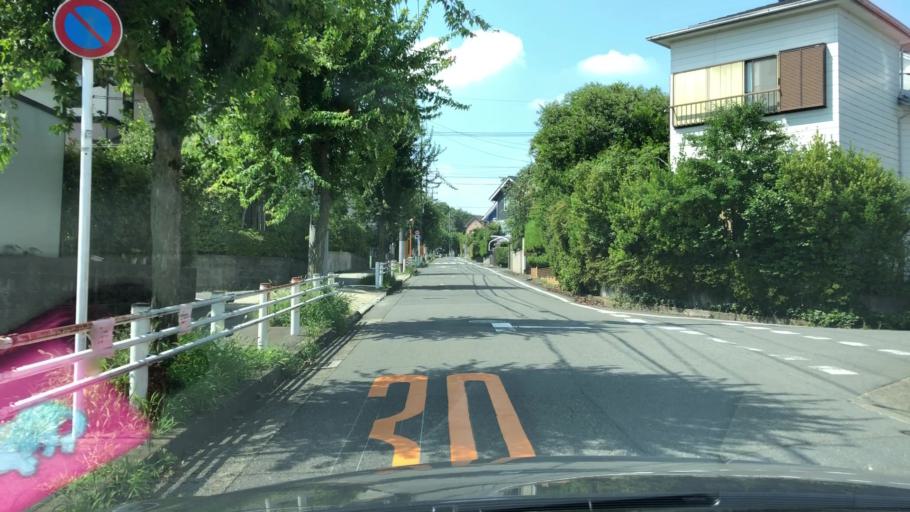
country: JP
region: Tokyo
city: Hino
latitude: 35.6891
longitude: 139.3575
